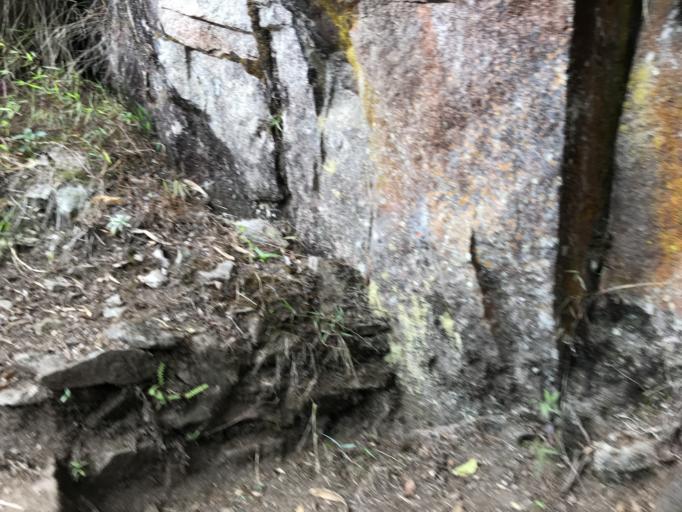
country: PE
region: Cusco
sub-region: Provincia de La Convencion
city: Santa Teresa
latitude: -13.1759
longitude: -72.5360
